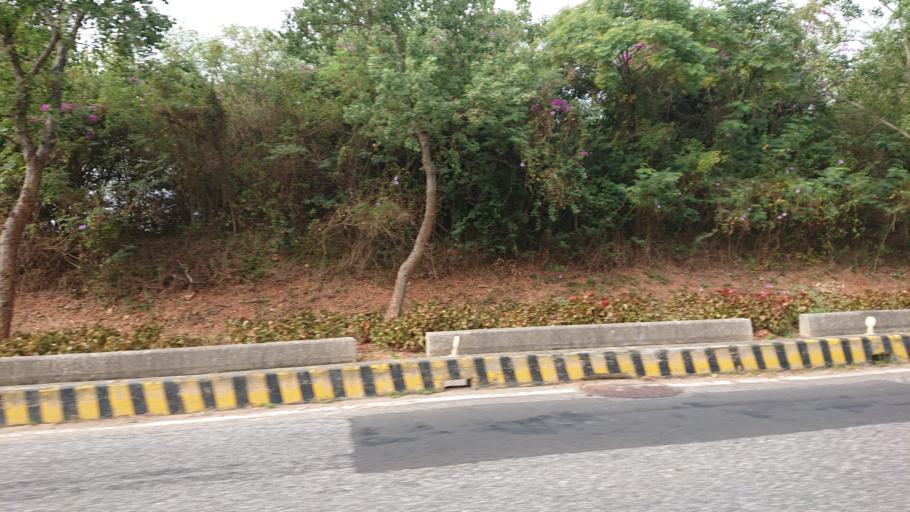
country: TW
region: Fukien
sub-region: Kinmen
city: Jincheng
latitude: 24.4739
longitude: 118.4110
